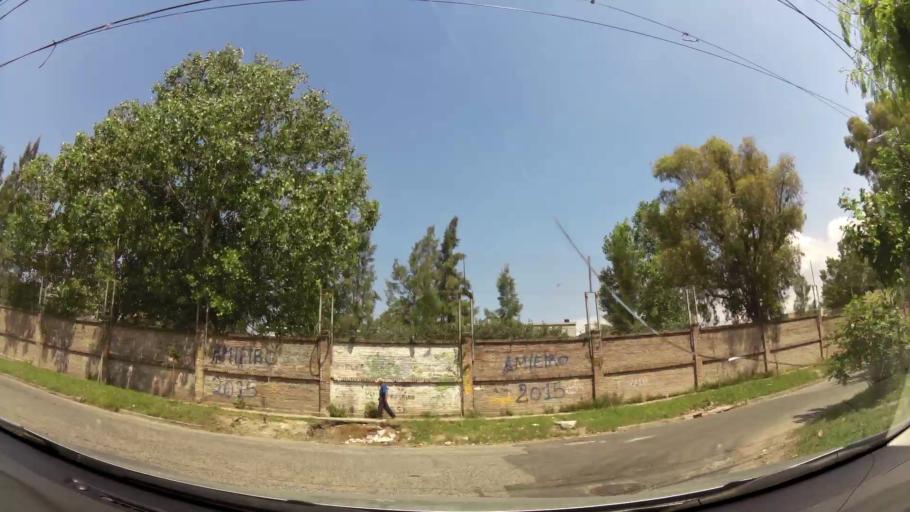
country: AR
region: Buenos Aires
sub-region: Partido de Tigre
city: Tigre
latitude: -34.4604
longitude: -58.5817
